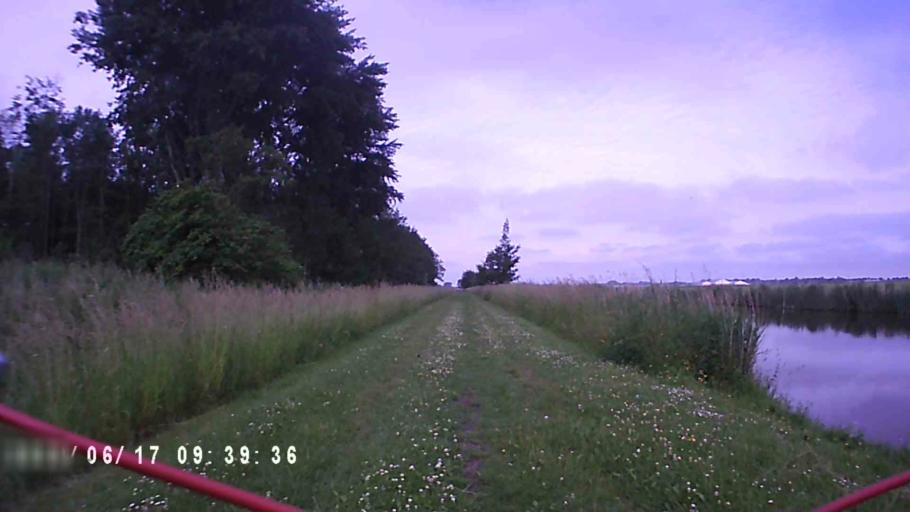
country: NL
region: Groningen
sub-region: Gemeente De Marne
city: Ulrum
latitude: 53.3518
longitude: 6.3663
